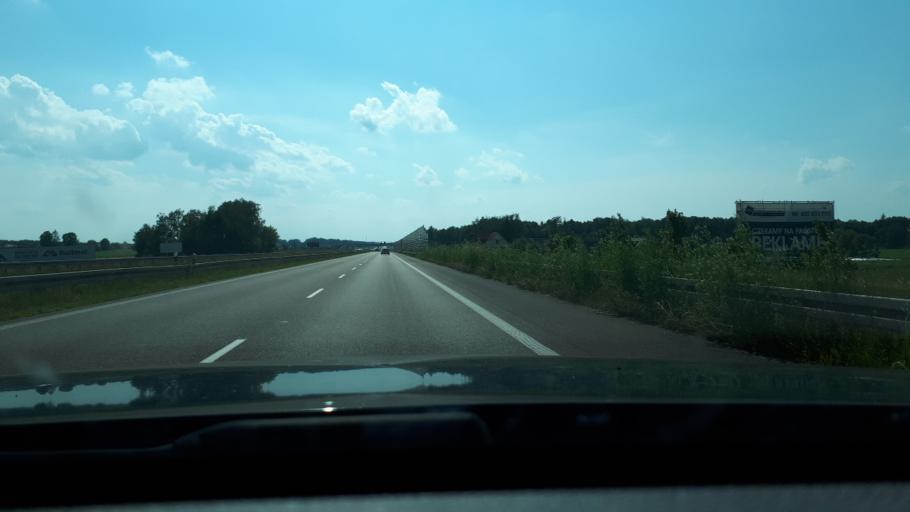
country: PL
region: Podlasie
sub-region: Powiat bialostocki
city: Choroszcz
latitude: 53.1635
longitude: 22.9170
